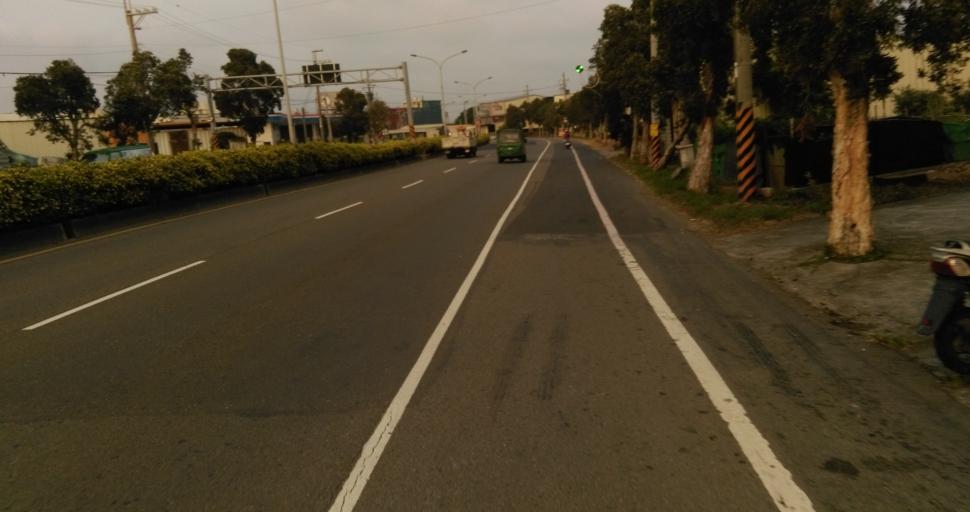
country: TW
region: Taiwan
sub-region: Hsinchu
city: Hsinchu
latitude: 24.8194
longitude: 120.9253
